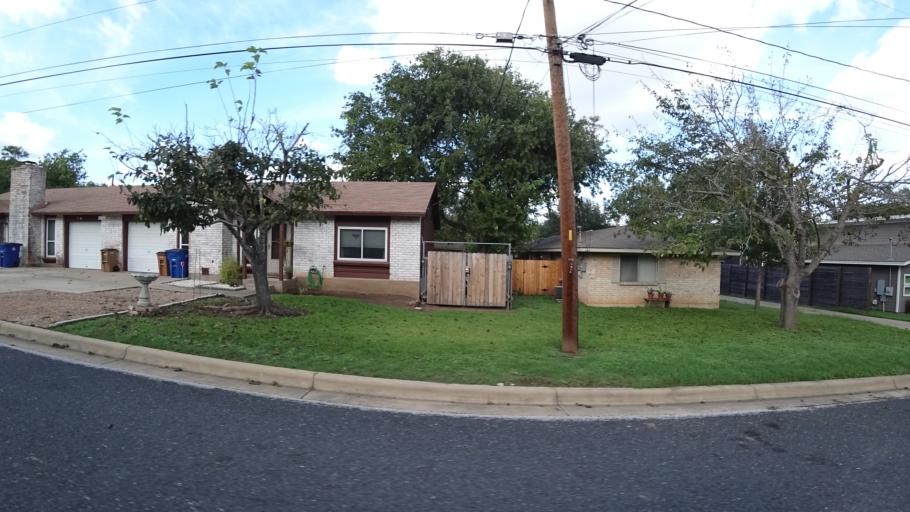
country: US
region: Texas
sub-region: Travis County
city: Rollingwood
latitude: 30.2068
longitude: -97.8011
